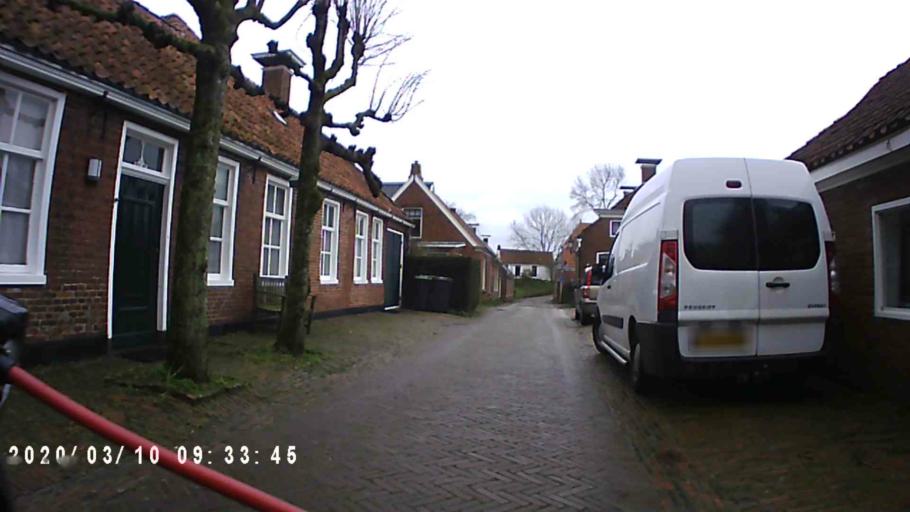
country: NL
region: Groningen
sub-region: Gemeente Winsum
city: Winsum
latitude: 53.3053
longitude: 6.4922
